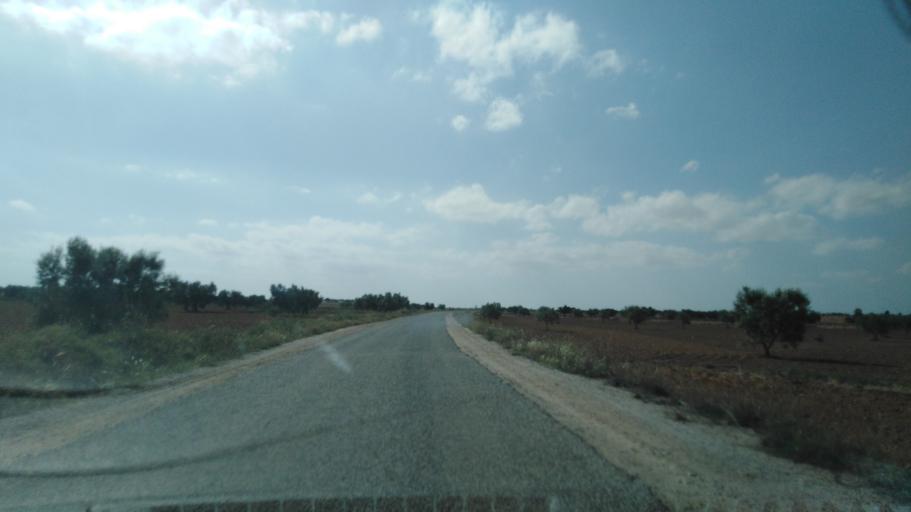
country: TN
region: Safaqis
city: Bi'r `Ali Bin Khalifah
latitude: 34.7778
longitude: 10.3585
